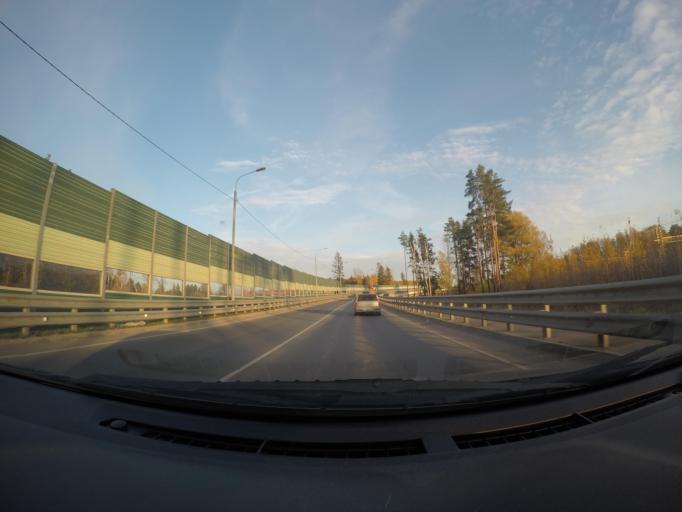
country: RU
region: Moskovskaya
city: Firsanovka
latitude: 55.9597
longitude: 37.2571
